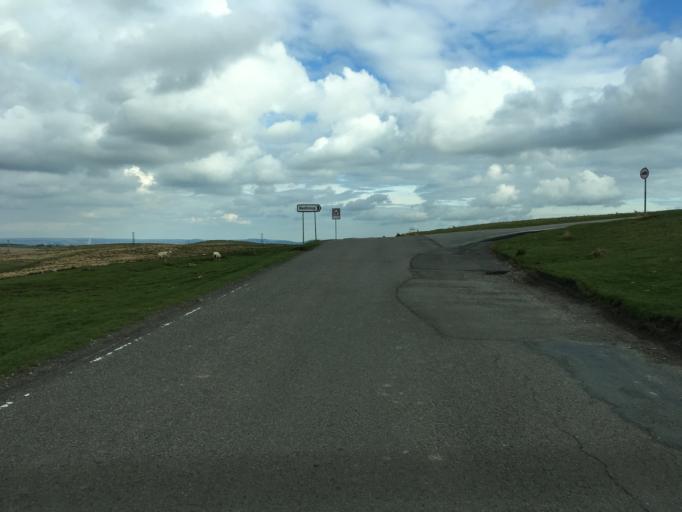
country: GB
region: Wales
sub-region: Caerphilly County Borough
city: Rhymney
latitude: 51.7208
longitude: -3.2955
